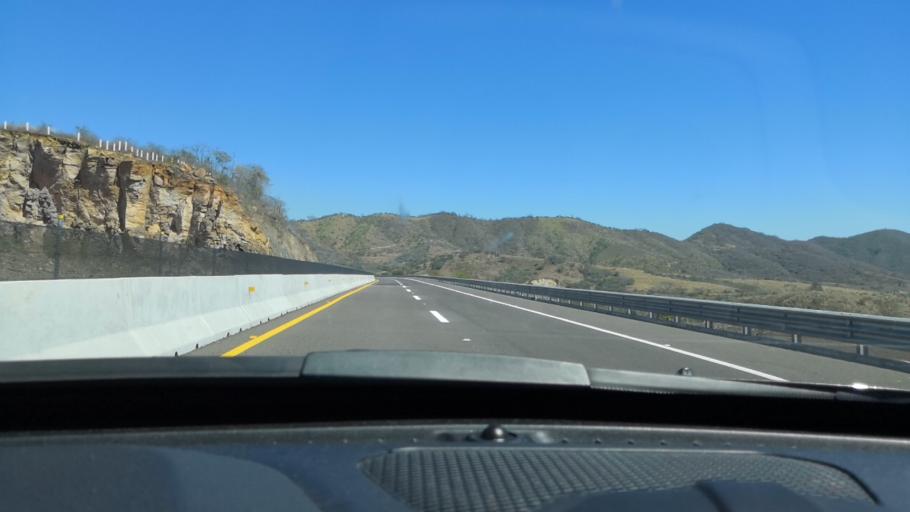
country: MX
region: Nayarit
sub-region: Compostela
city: Juan Escutia (Borbollon)
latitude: 21.1166
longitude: -104.8817
